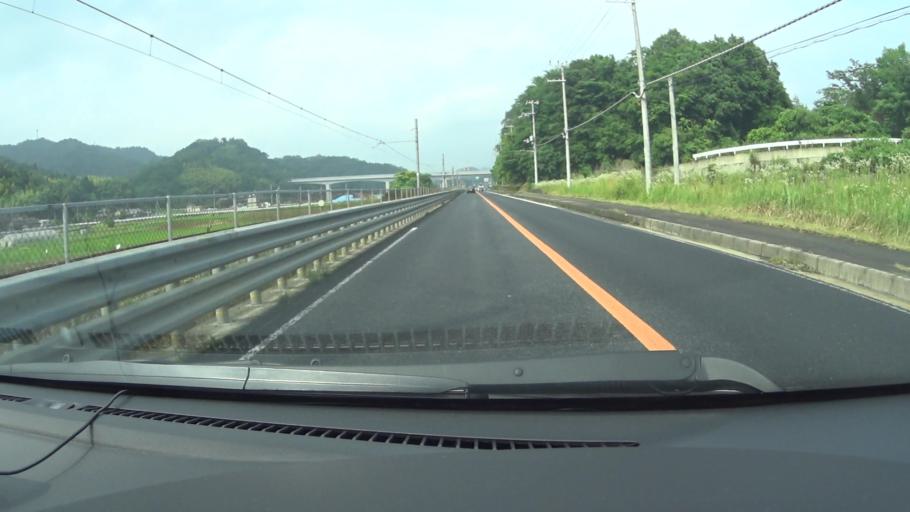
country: JP
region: Kyoto
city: Ayabe
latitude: 35.3341
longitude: 135.3027
